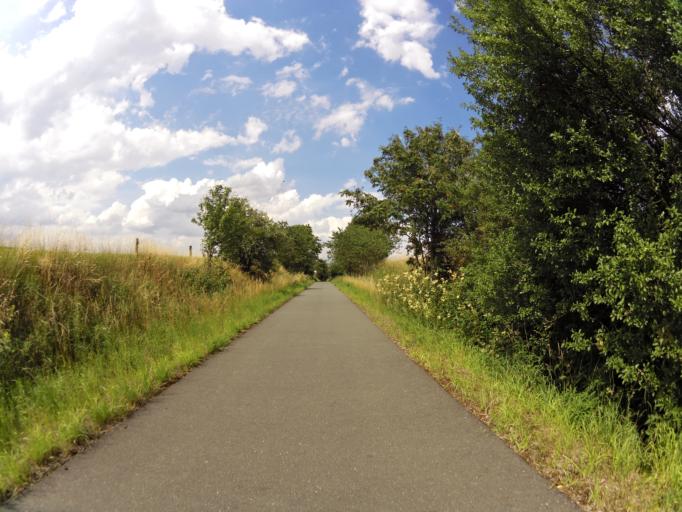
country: DE
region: Thuringia
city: Burgk
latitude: 50.5391
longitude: 11.7579
